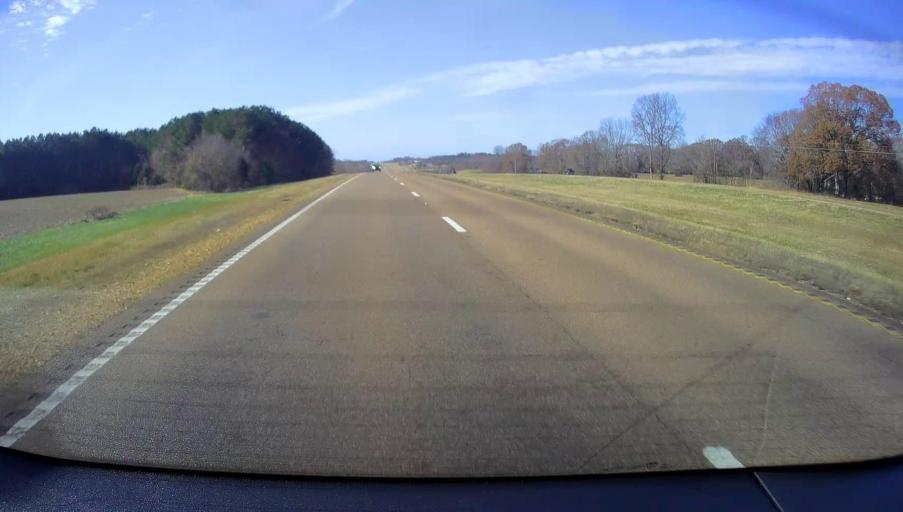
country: US
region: Mississippi
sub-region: Marshall County
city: Holly Springs
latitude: 34.9461
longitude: -89.3667
